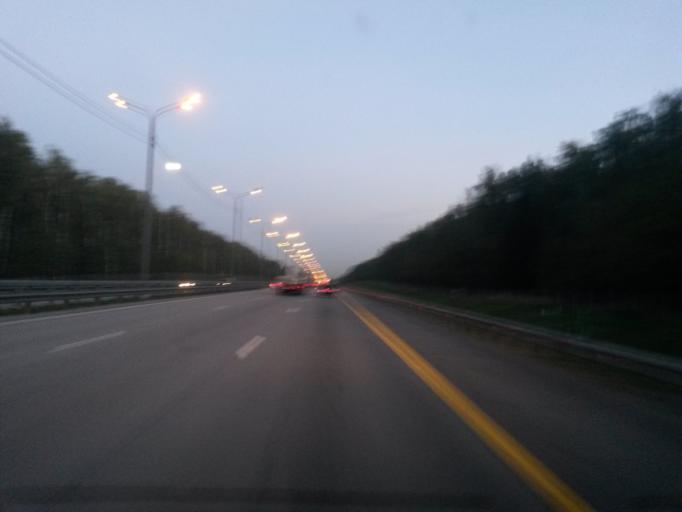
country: RU
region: Moskovskaya
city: Belyye Stolby
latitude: 55.3010
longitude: 37.8362
